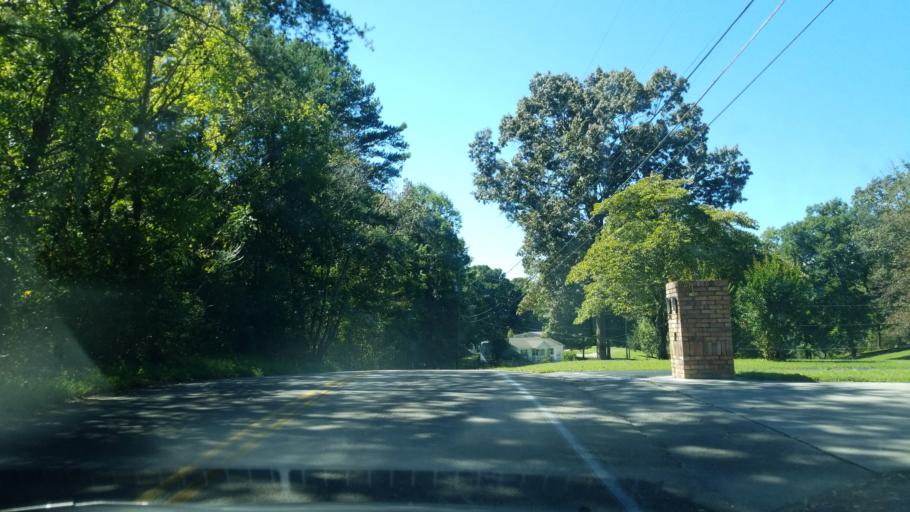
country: US
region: Tennessee
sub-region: Hamilton County
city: Collegedale
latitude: 35.0959
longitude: -85.0815
